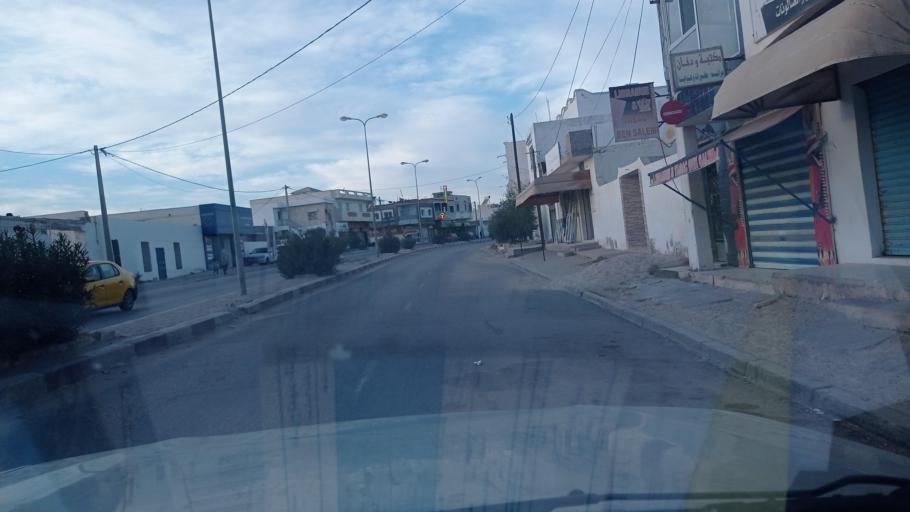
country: TN
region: Qabis
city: Gabes
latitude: 33.8408
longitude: 10.1145
